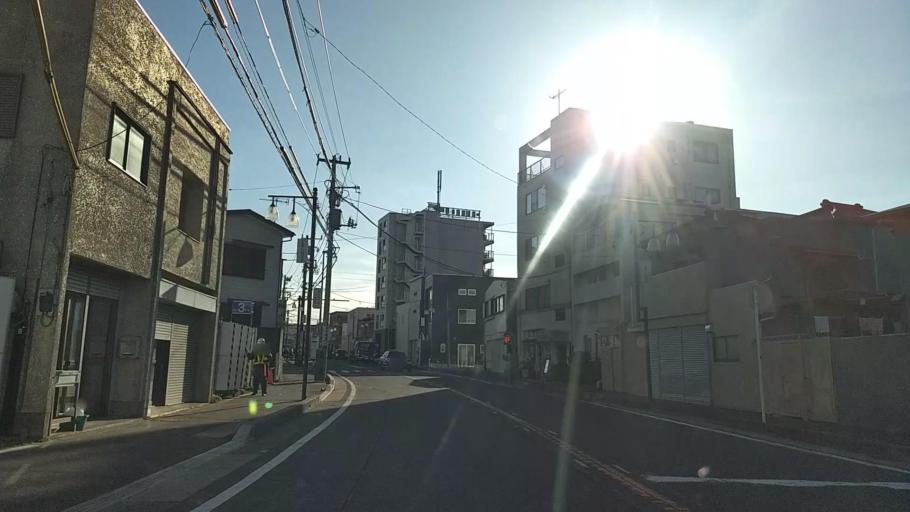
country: JP
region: Kanagawa
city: Fujisawa
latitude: 35.3115
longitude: 139.4873
